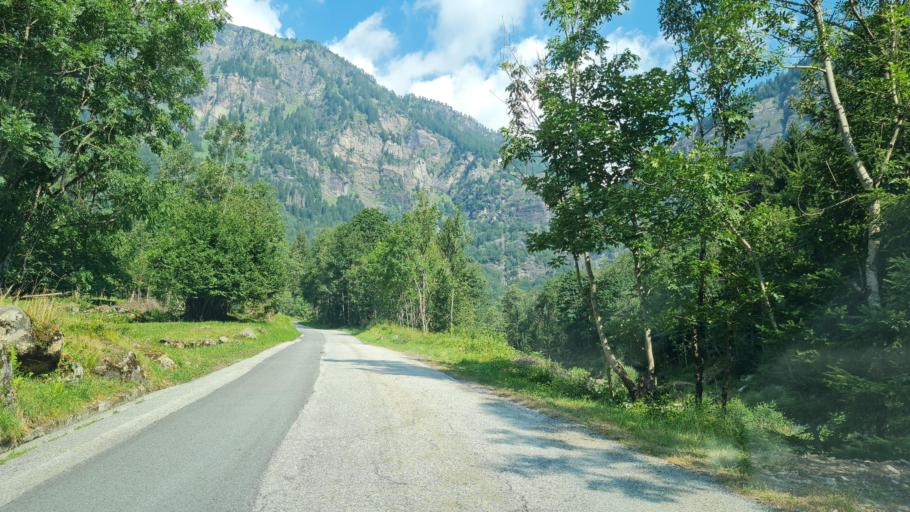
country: IT
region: Piedmont
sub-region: Provincia Verbano-Cusio-Ossola
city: Baceno
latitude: 46.2904
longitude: 8.2708
